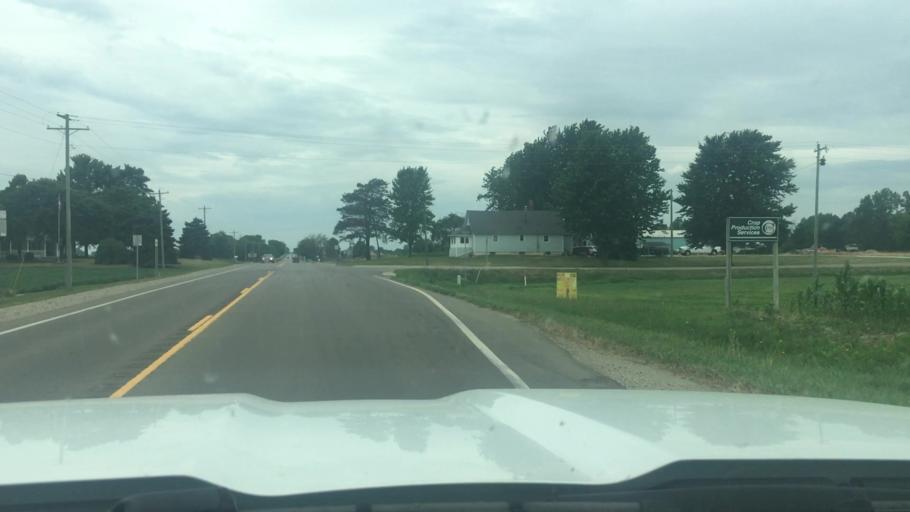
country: US
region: Michigan
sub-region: Clinton County
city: Fowler
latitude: 43.0017
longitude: -84.6793
